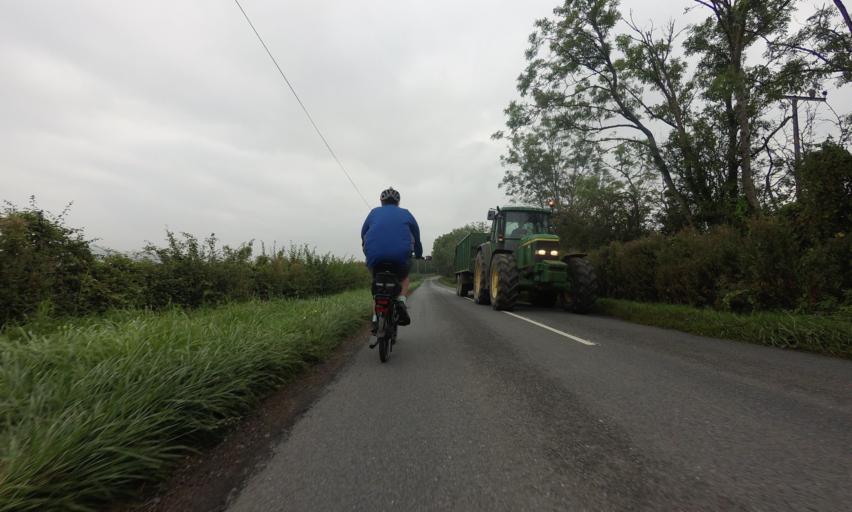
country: GB
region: England
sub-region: Gloucestershire
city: Gotherington
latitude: 51.9719
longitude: -2.0112
